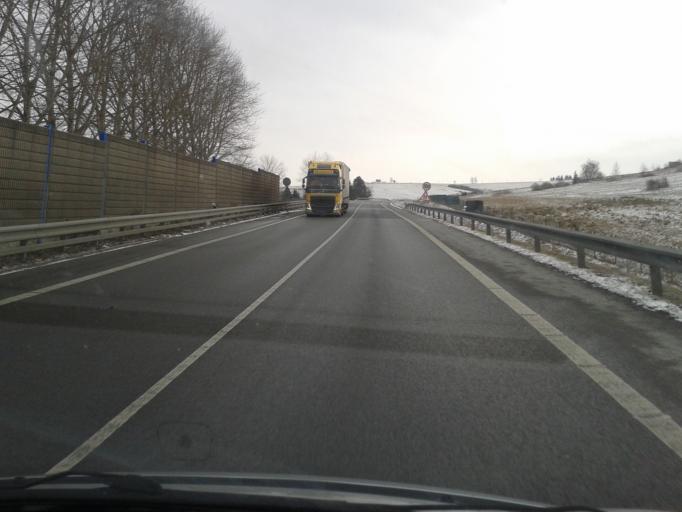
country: SK
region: Zilinsky
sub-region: Okres Zilina
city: Trstena
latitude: 49.3518
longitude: 19.6080
